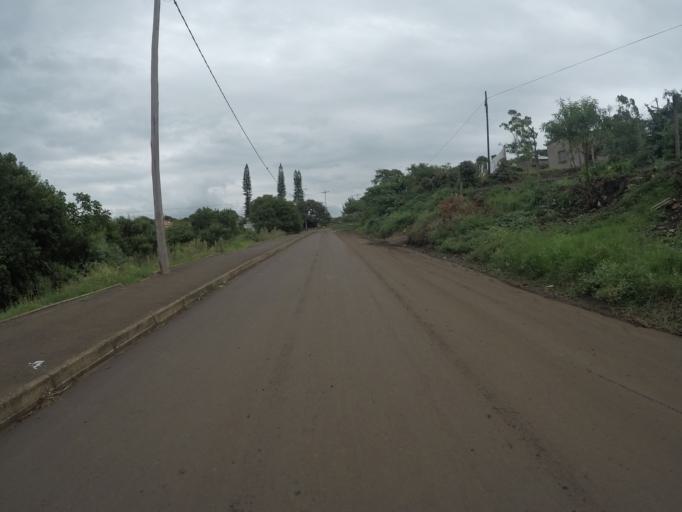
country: ZA
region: KwaZulu-Natal
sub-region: uThungulu District Municipality
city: Empangeni
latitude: -28.7718
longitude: 31.8569
